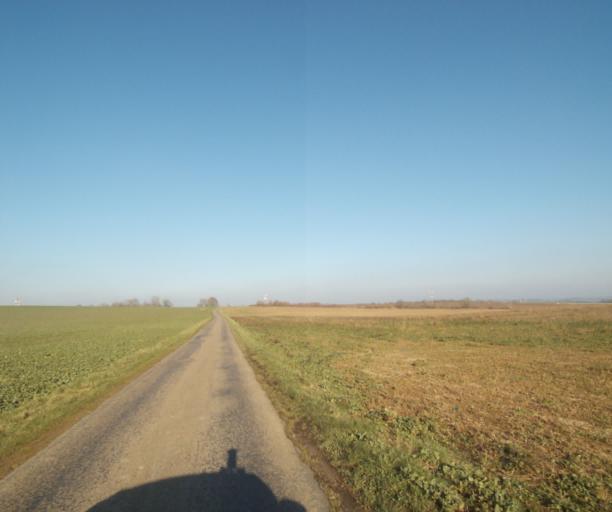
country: FR
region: Champagne-Ardenne
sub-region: Departement de la Haute-Marne
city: Chevillon
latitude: 48.5099
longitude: 5.0858
